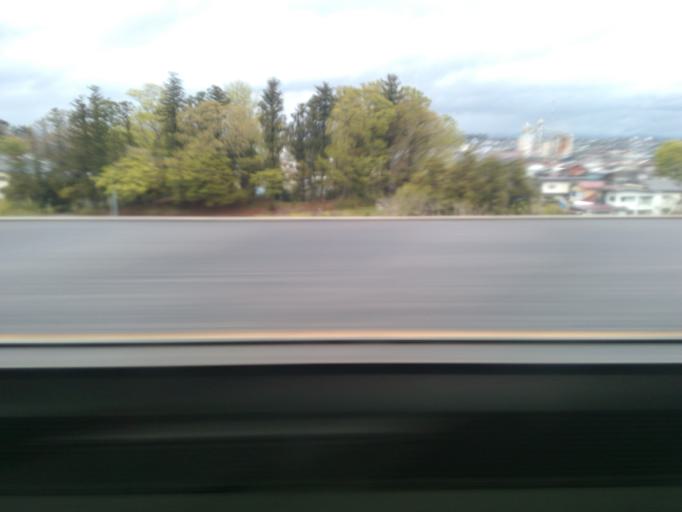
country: JP
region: Fukushima
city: Koriyama
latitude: 37.3500
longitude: 140.3712
